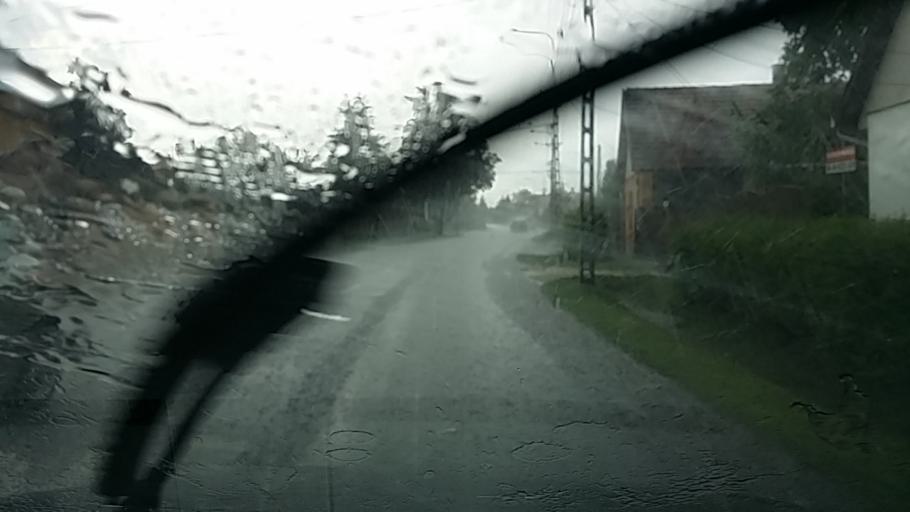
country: HU
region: Pest
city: Ocsa
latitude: 47.2929
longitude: 19.2330
